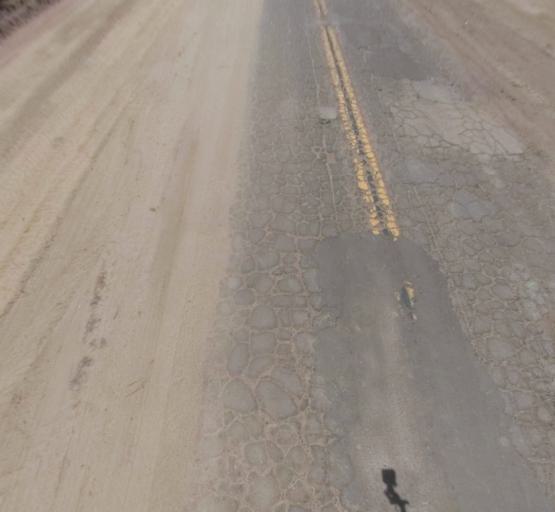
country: US
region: California
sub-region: Madera County
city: Chowchilla
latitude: 37.0692
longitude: -120.4191
